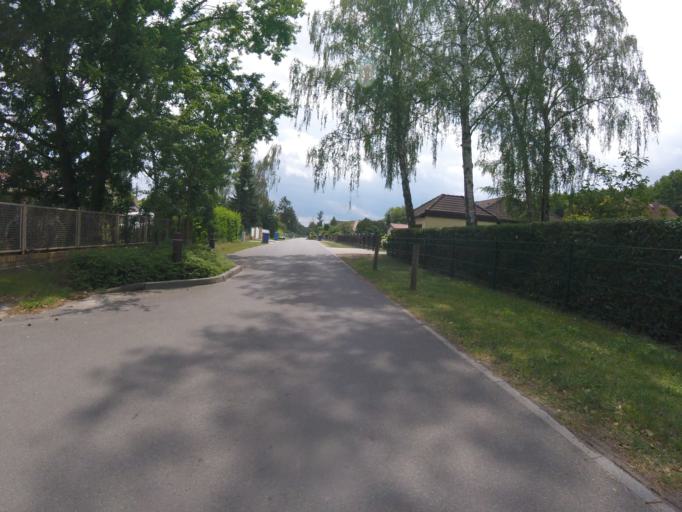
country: DE
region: Brandenburg
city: Bestensee
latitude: 52.2638
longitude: 13.6416
